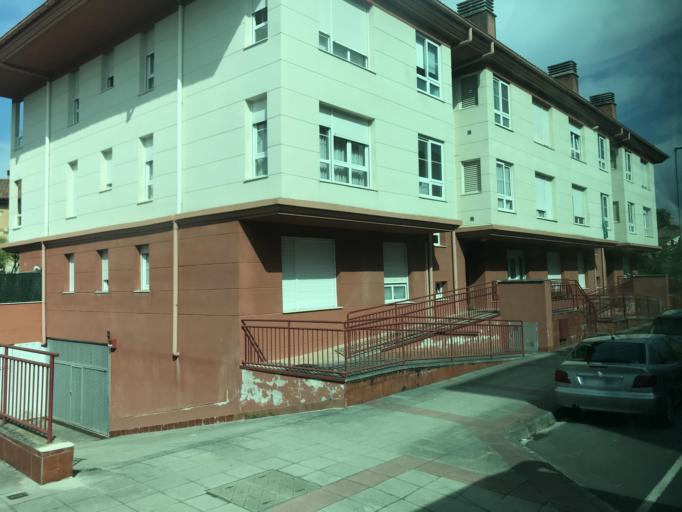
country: ES
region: Basque Country
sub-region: Bizkaia
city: Otxandio
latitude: 43.0423
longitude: -2.6538
